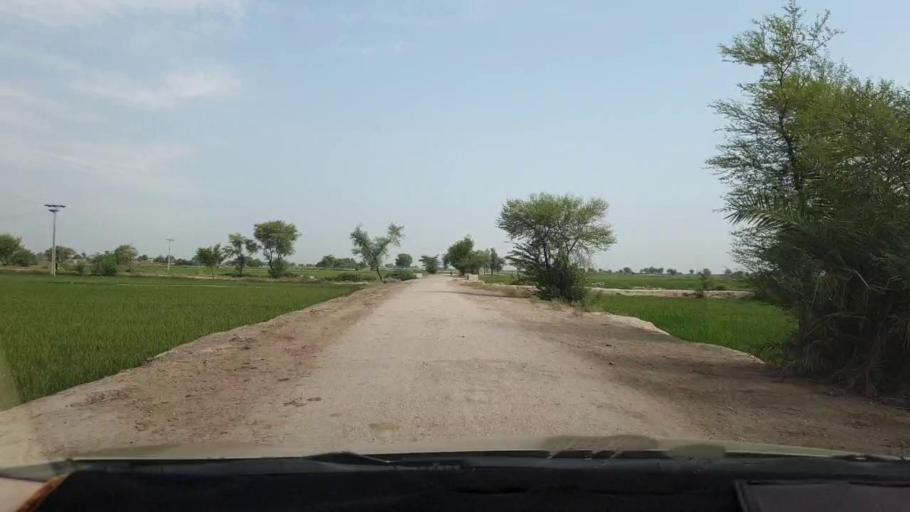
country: PK
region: Sindh
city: Larkana
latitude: 27.6749
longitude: 68.2202
